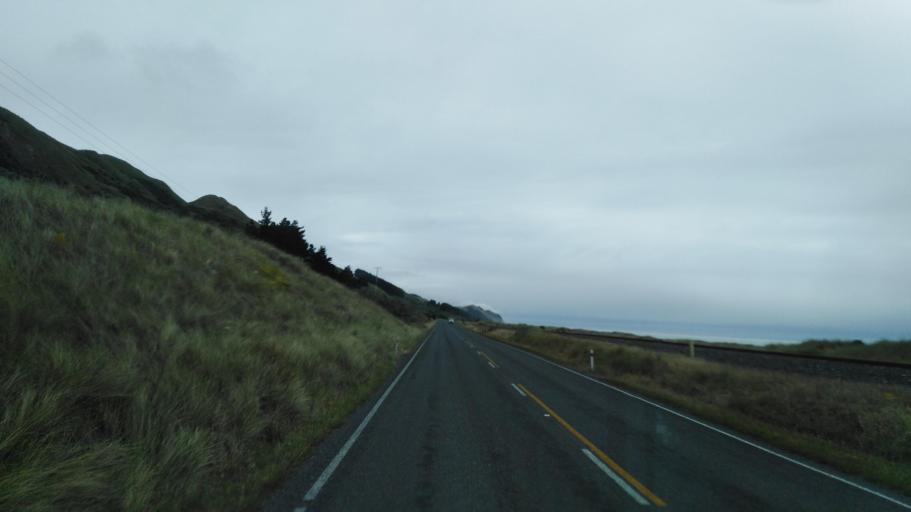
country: NZ
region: Canterbury
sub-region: Kaikoura District
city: Kaikoura
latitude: -42.0440
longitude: 173.9663
